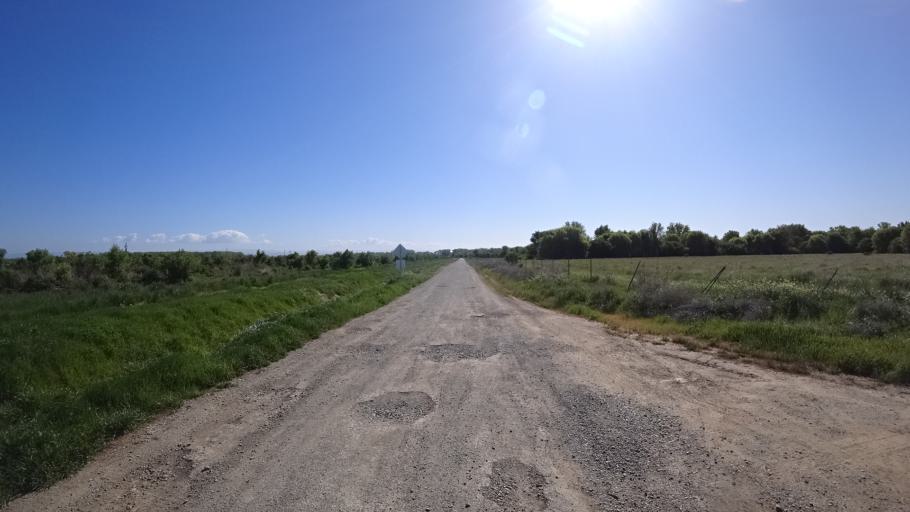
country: US
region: California
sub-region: Glenn County
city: Hamilton City
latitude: 39.7127
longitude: -121.9687
